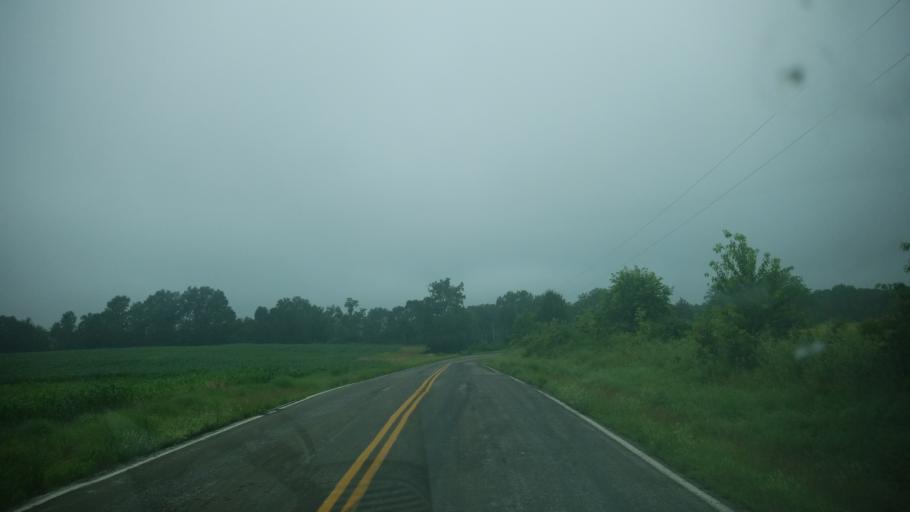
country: US
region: Missouri
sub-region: Audrain County
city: Vandalia
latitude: 39.2876
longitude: -91.3478
